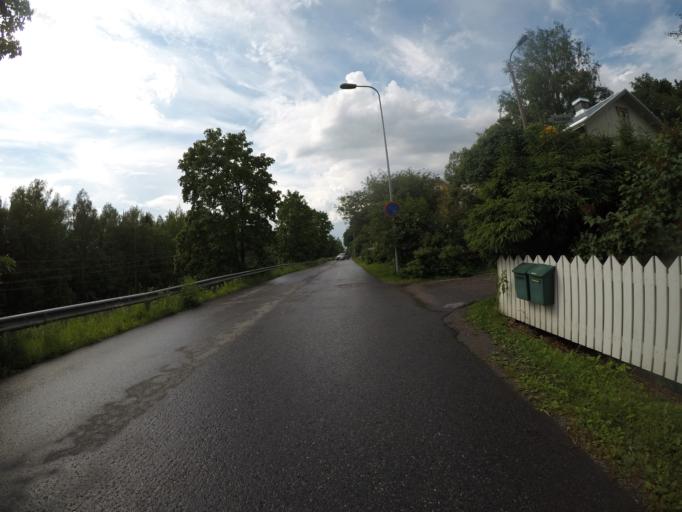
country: FI
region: Haeme
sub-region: Haemeenlinna
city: Haemeenlinna
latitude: 61.0044
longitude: 24.4744
